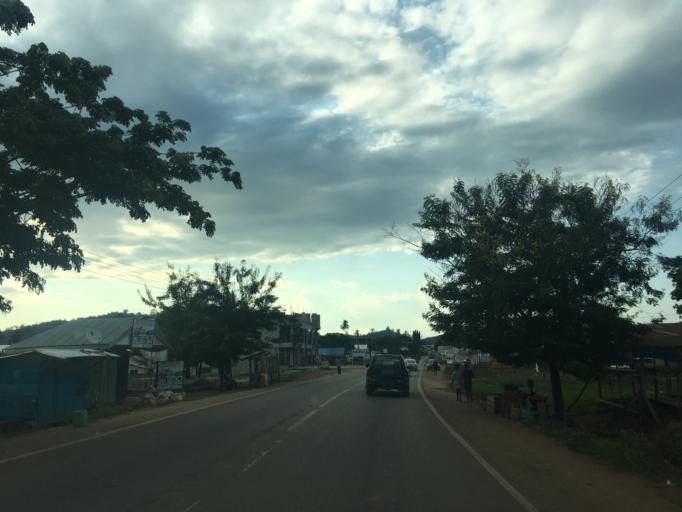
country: GH
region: Western
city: Bibiani
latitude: 6.4420
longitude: -2.3128
